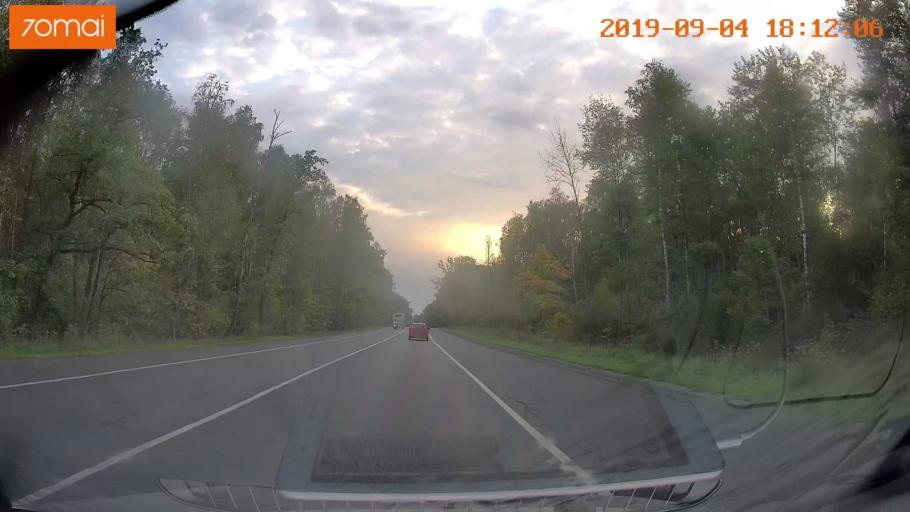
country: RU
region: Moskovskaya
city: Lopatinskiy
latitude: 55.3727
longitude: 38.7468
